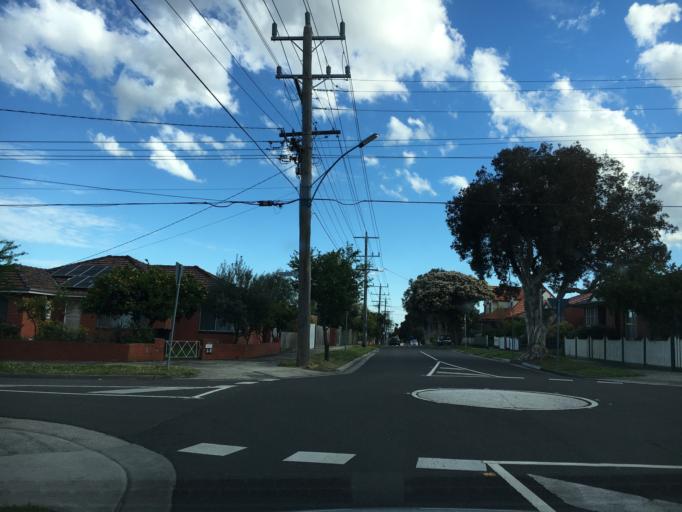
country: AU
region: Victoria
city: Clayton
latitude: -37.9149
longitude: 145.1163
